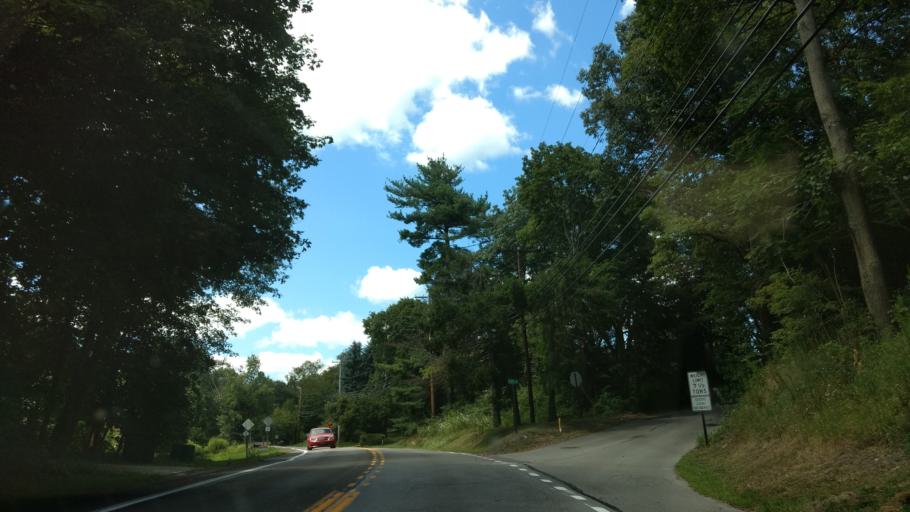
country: US
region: Pennsylvania
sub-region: Beaver County
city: Beaver
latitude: 40.7031
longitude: -80.3129
